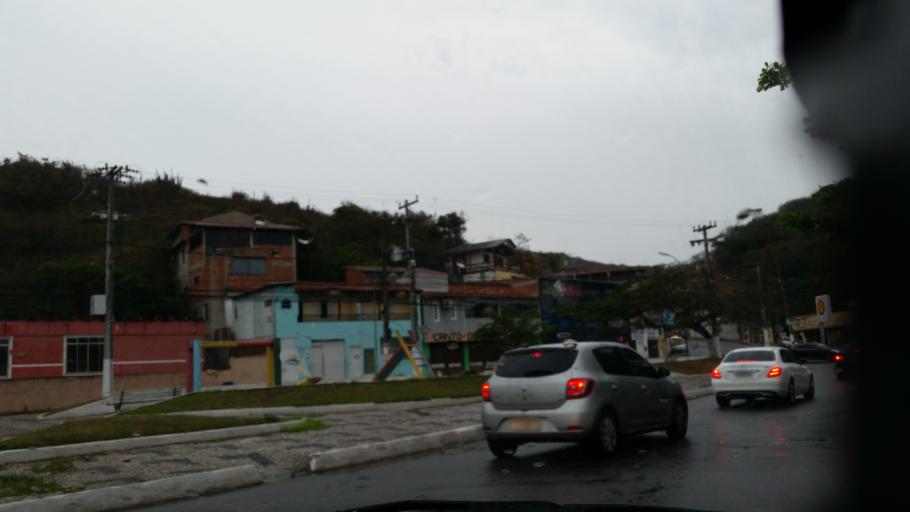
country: BR
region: Rio de Janeiro
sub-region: Cabo Frio
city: Cabo Frio
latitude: -22.8670
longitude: -42.0147
